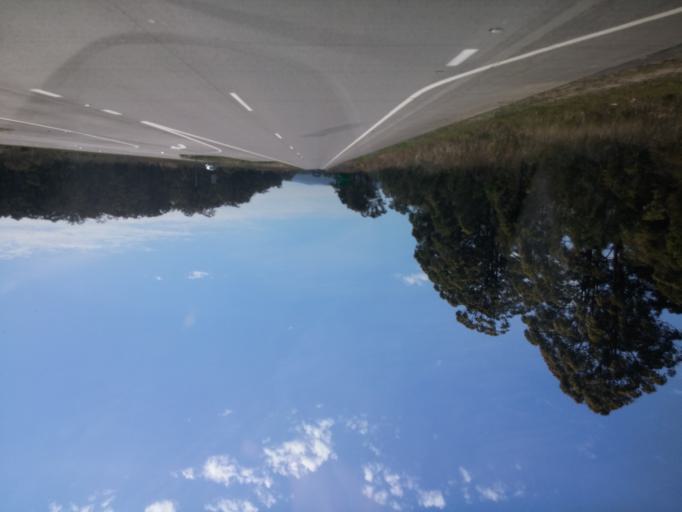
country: AU
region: New South Wales
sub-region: Great Lakes
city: Bulahdelah
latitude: -32.4491
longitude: 152.1964
